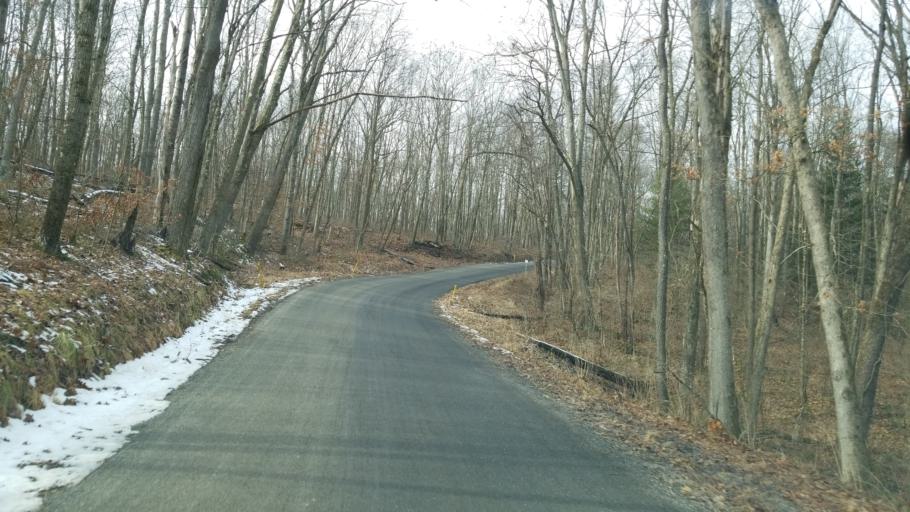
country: US
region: Pennsylvania
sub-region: Jefferson County
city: Punxsutawney
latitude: 40.8741
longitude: -79.0565
